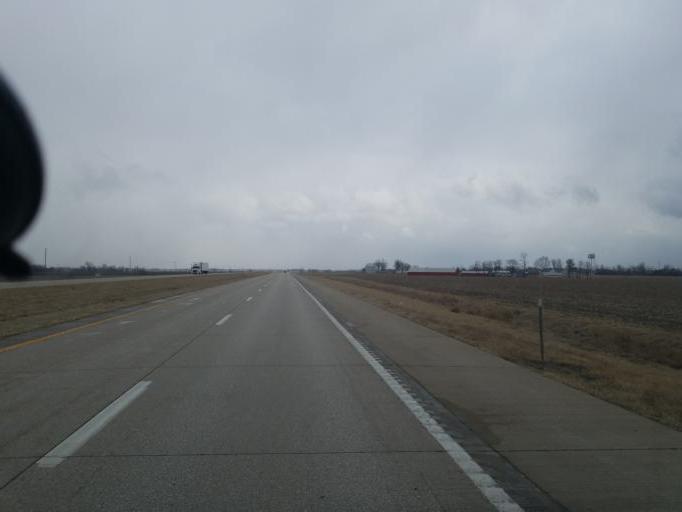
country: US
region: Missouri
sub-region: Randolph County
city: Moberly
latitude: 39.5275
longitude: -92.4420
